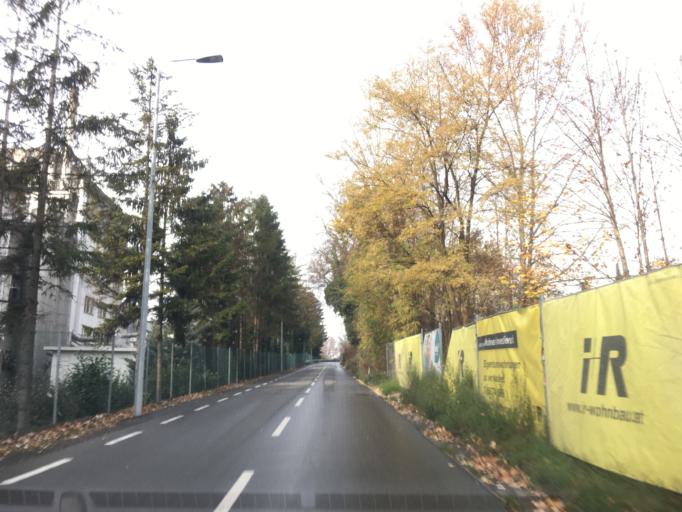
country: AT
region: Vorarlberg
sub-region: Politischer Bezirk Bludenz
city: Bludenz
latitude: 47.1562
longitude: 9.8161
